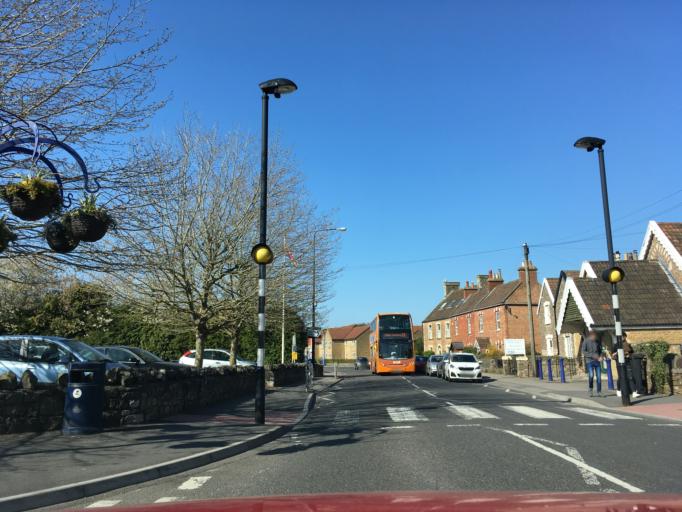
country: GB
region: England
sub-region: North Somerset
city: Portishead
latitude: 51.4806
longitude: -2.7683
